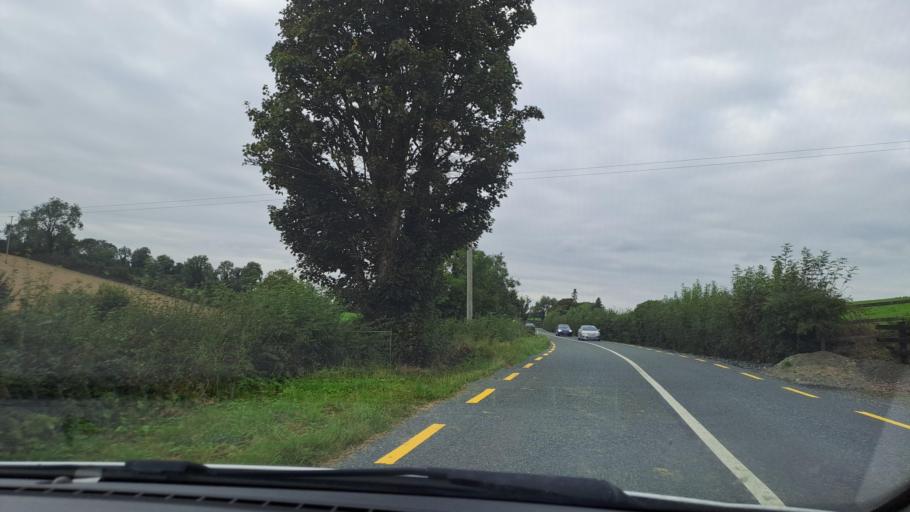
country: IE
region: Ulster
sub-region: An Cabhan
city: Kingscourt
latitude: 53.9747
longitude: -6.8733
